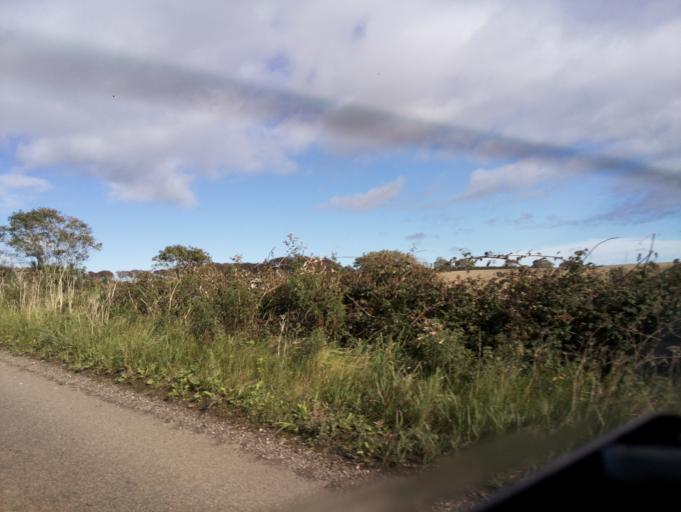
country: GB
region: England
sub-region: Devon
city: Kingsbridge
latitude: 50.3088
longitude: -3.7779
